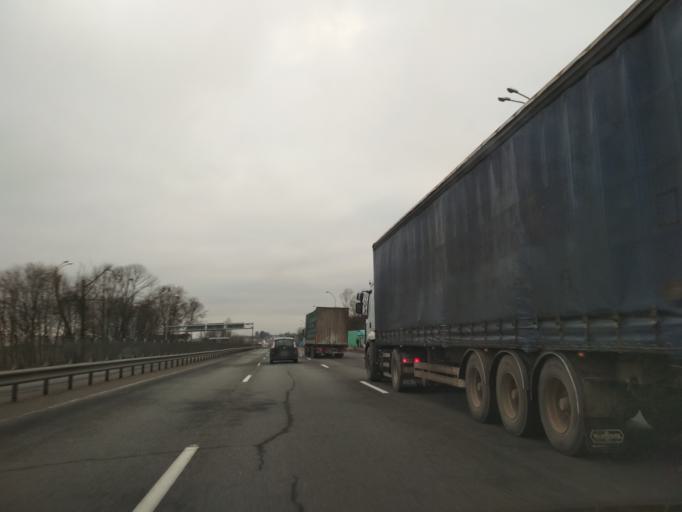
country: BY
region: Minsk
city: Pryvol'ny
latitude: 53.8011
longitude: 27.8011
